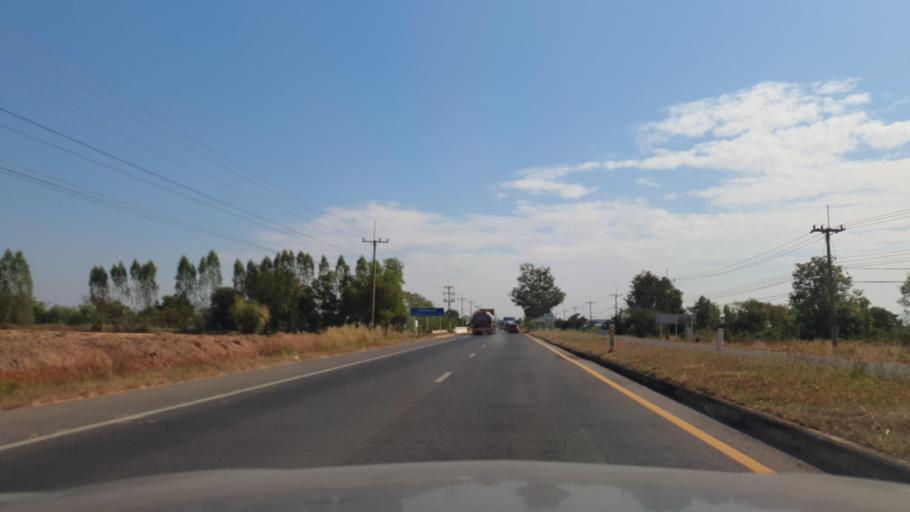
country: TH
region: Maha Sarakham
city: Chiang Yuen
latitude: 16.3758
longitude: 103.1665
